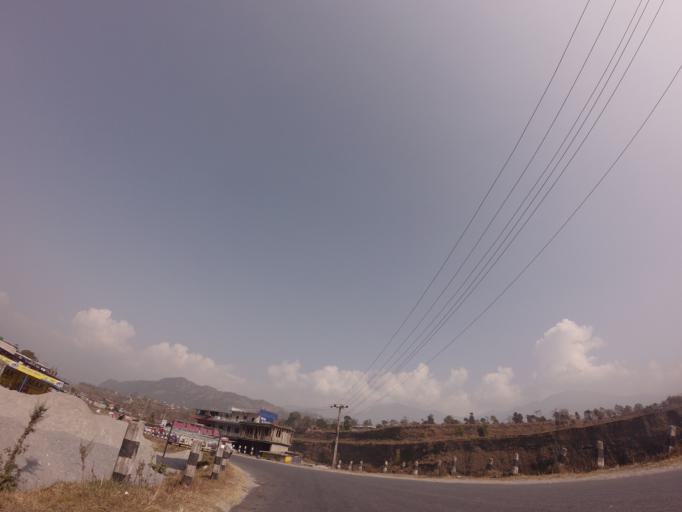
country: NP
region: Western Region
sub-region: Gandaki Zone
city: Pokhara
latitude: 28.2537
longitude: 83.9666
